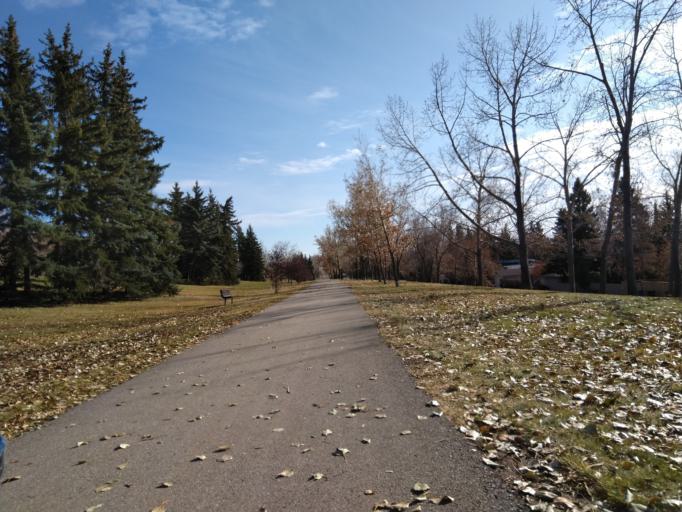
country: CA
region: Alberta
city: Calgary
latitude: 51.0981
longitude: -114.1199
